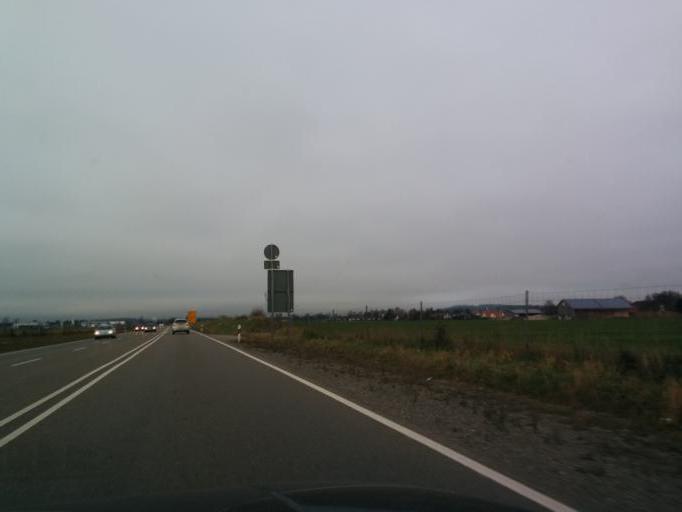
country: DE
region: Bavaria
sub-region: Swabia
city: Mauerstetten
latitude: 47.9154
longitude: 10.6585
